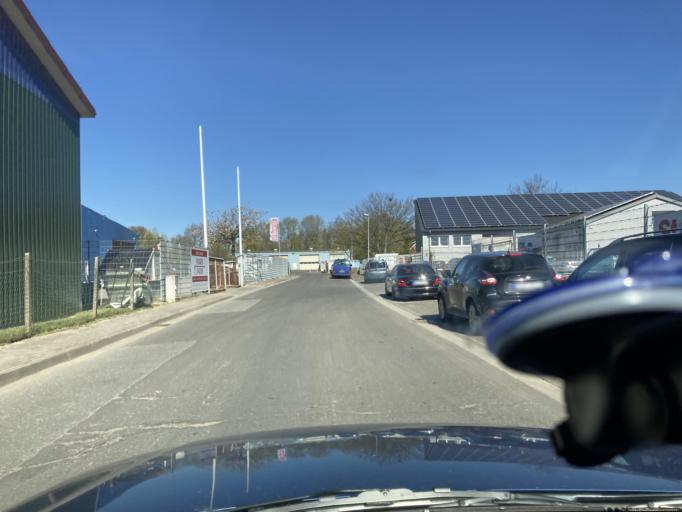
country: DE
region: Schleswig-Holstein
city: Heide
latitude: 54.1841
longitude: 9.1048
